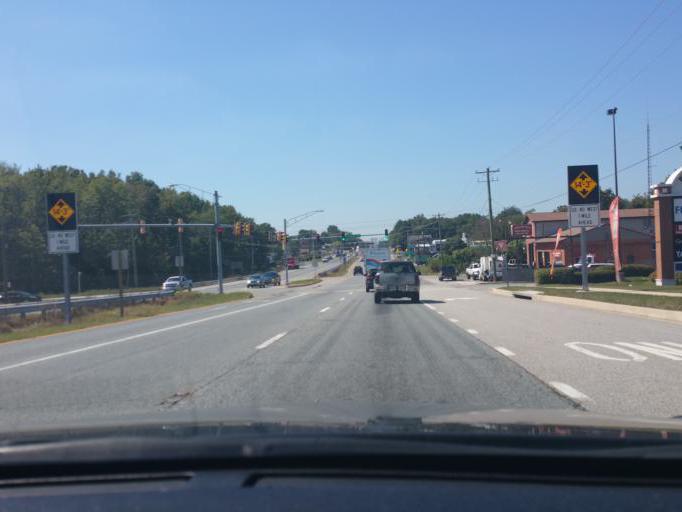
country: US
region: Maryland
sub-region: Cecil County
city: Perryville
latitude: 39.5716
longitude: -76.0661
